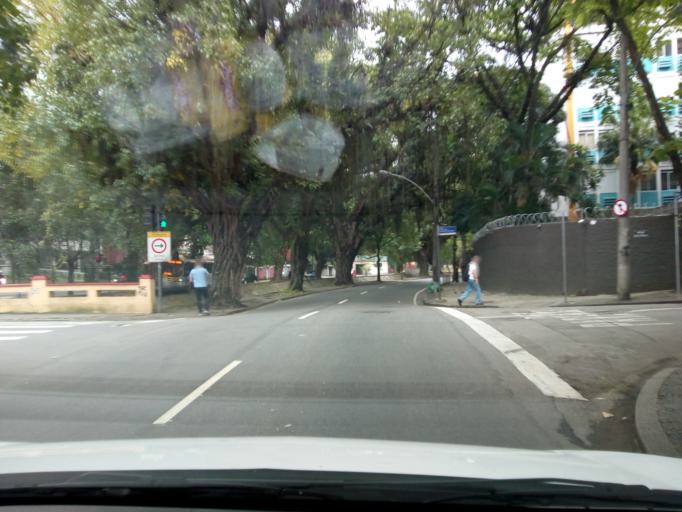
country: BR
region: Rio de Janeiro
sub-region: Rio De Janeiro
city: Rio de Janeiro
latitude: -22.9850
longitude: -43.2294
